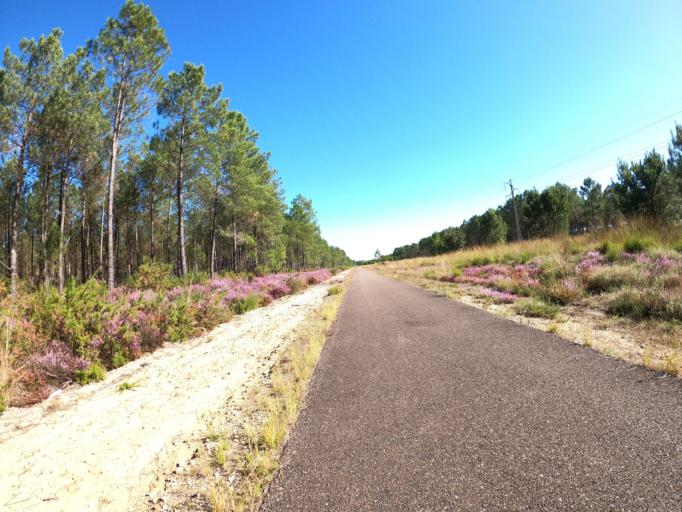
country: FR
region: Aquitaine
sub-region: Departement des Landes
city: Ychoux
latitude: 44.3399
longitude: -0.9648
